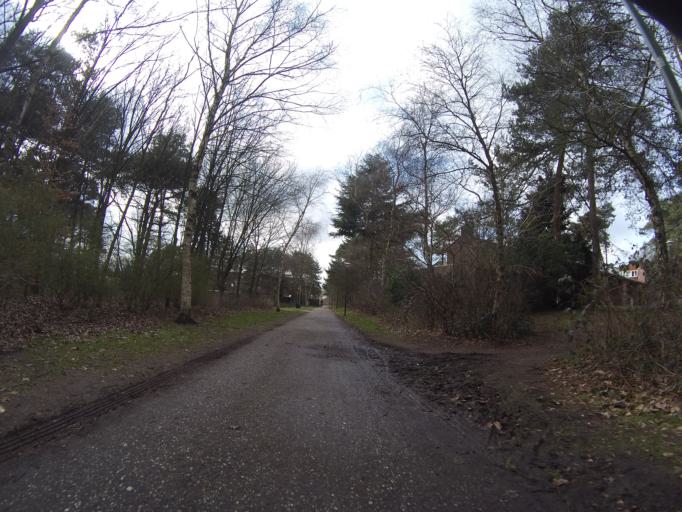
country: NL
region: Utrecht
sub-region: Gemeente Soest
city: Soest
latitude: 52.1164
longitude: 5.2981
